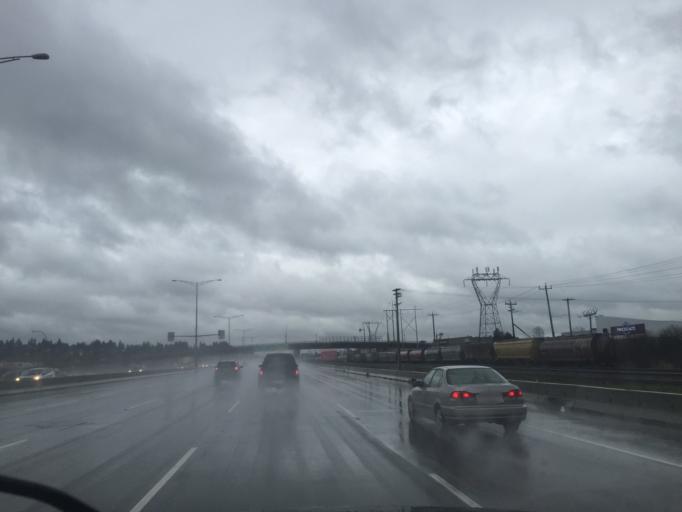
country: CA
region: British Columbia
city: New Westminster
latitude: 49.2327
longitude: -122.8664
